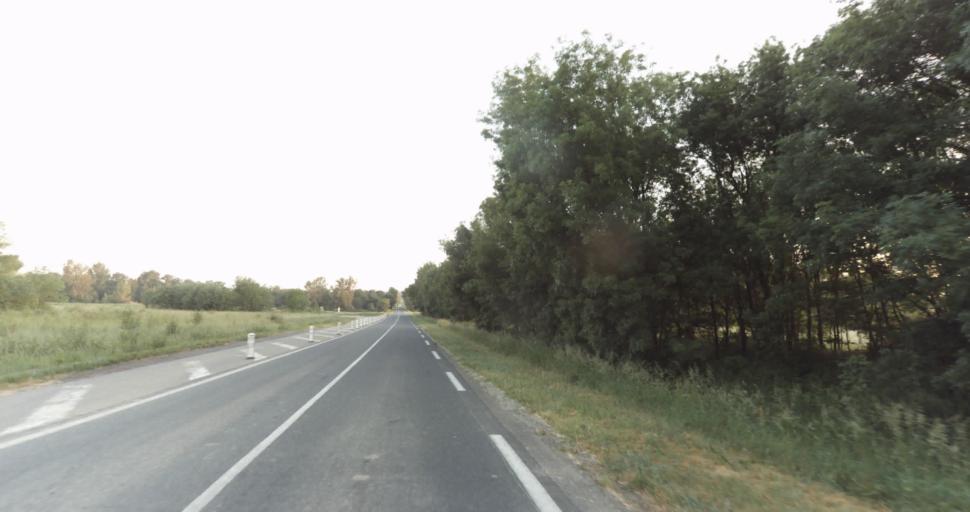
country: FR
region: Midi-Pyrenees
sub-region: Departement du Gers
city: Pujaudran
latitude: 43.6451
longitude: 1.1392
